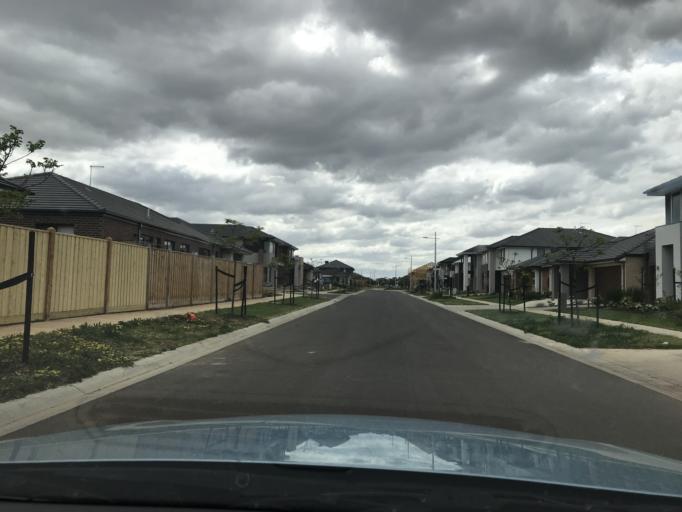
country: AU
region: Victoria
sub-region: Wyndham
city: Williams Landing
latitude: -37.8630
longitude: 144.7567
